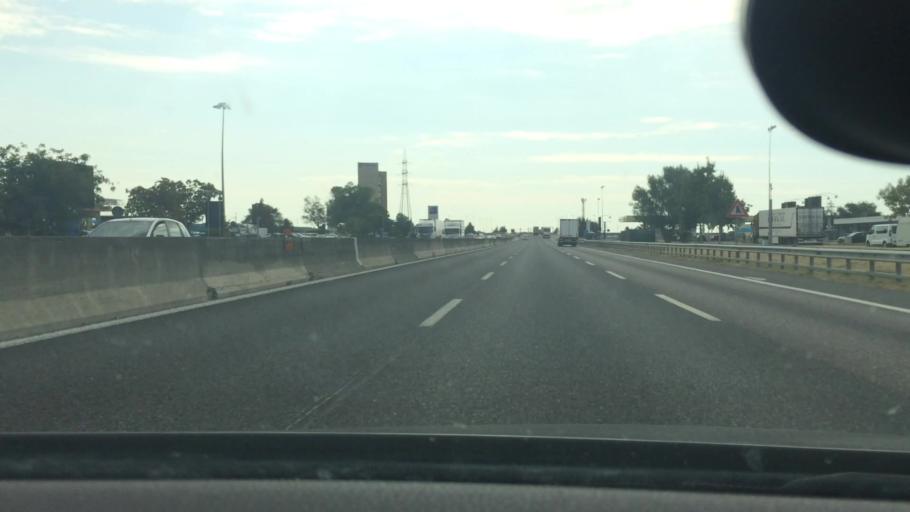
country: IT
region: Emilia-Romagna
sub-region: Provincia di Parma
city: San Prospero
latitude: 44.8272
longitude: 10.3775
